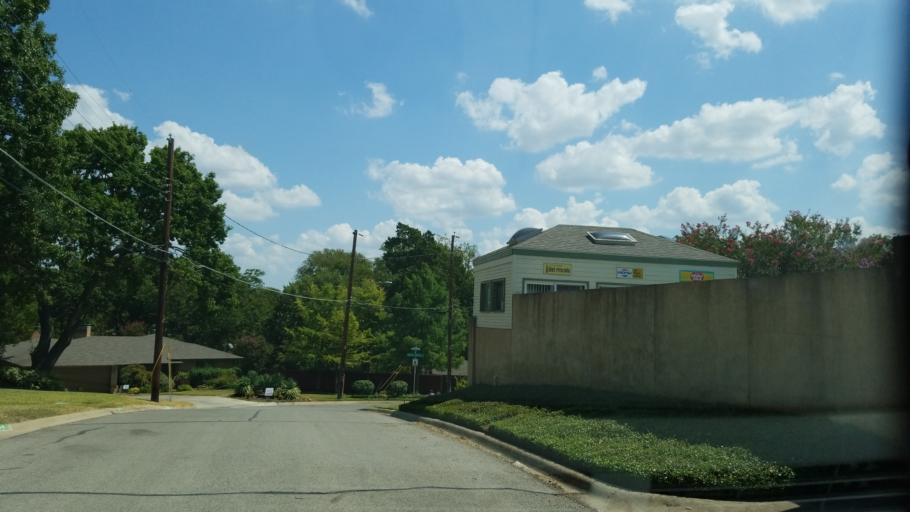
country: US
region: Texas
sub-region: Dallas County
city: Cockrell Hill
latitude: 32.7543
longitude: -96.8535
